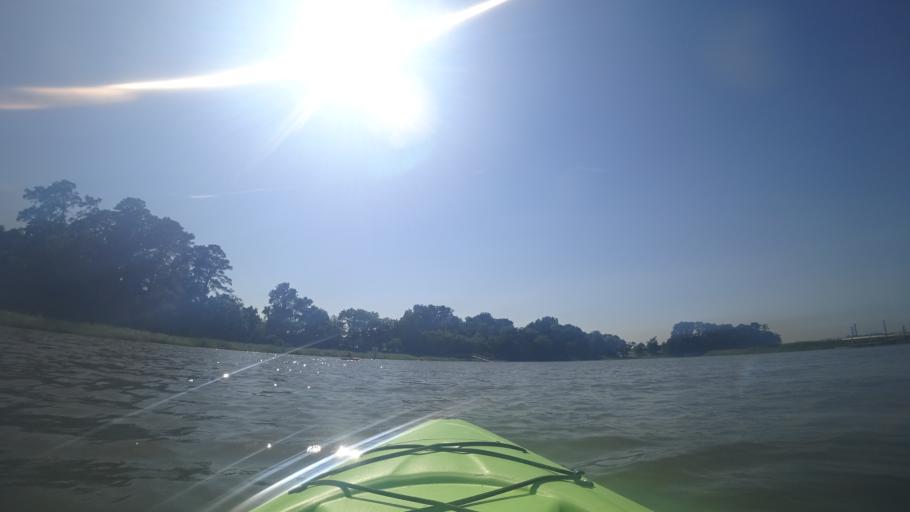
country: US
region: Virginia
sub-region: Isle of Wight County
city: Smithfield
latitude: 36.9747
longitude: -76.6205
